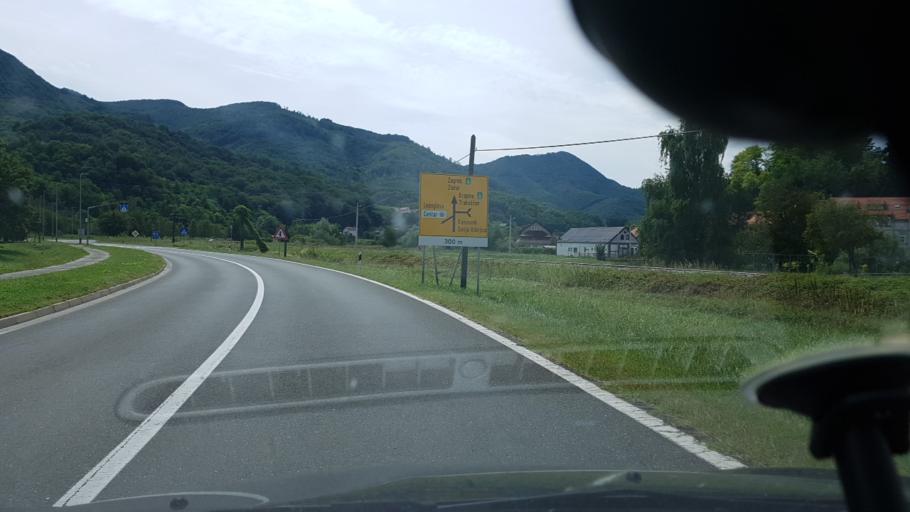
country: HR
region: Varazdinska
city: Lepoglava
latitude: 46.2102
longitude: 16.0373
